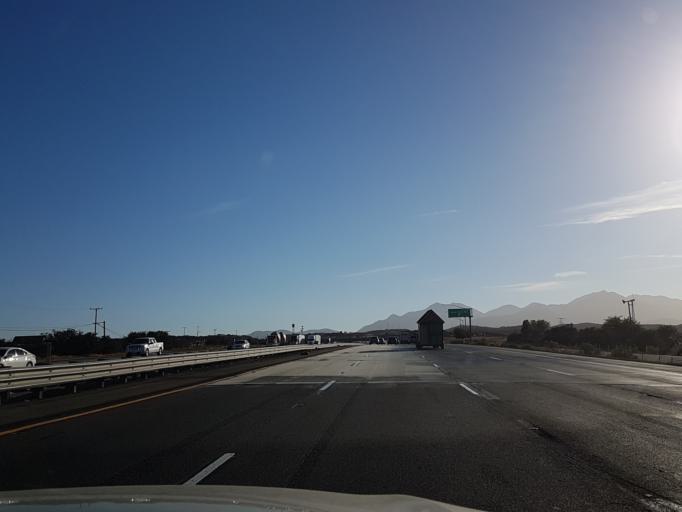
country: US
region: California
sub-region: San Bernardino County
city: Oak Hills
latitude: 34.3665
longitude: -117.4297
